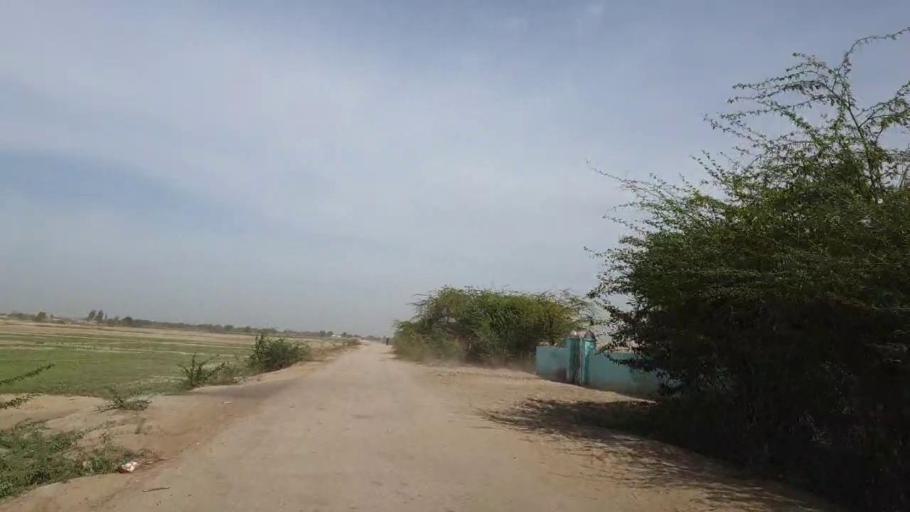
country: PK
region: Sindh
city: Kunri
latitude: 25.1695
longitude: 69.6175
